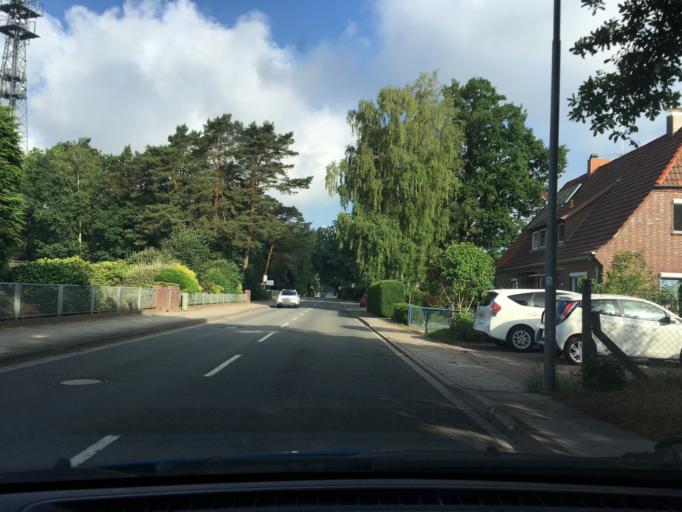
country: DE
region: Lower Saxony
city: Buchholz in der Nordheide
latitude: 53.3263
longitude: 9.8426
